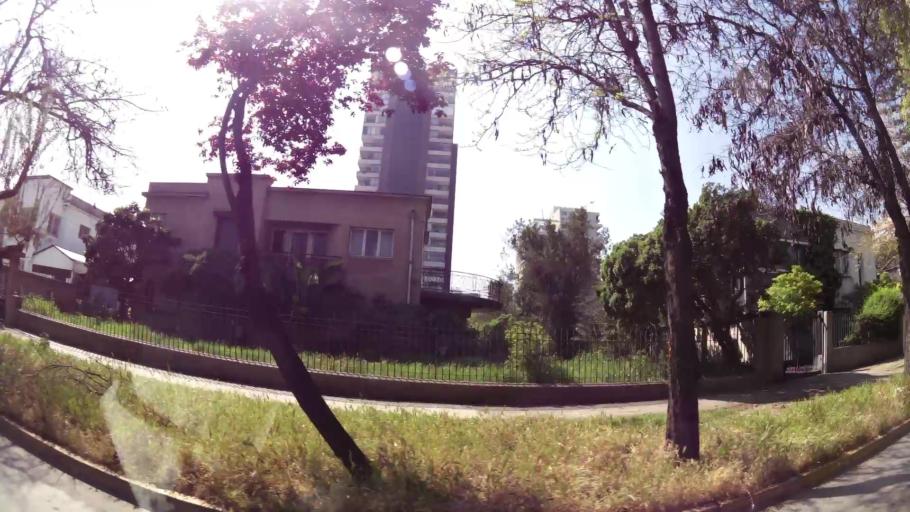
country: CL
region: Santiago Metropolitan
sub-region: Provincia de Santiago
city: Santiago
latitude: -33.4573
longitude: -70.6152
